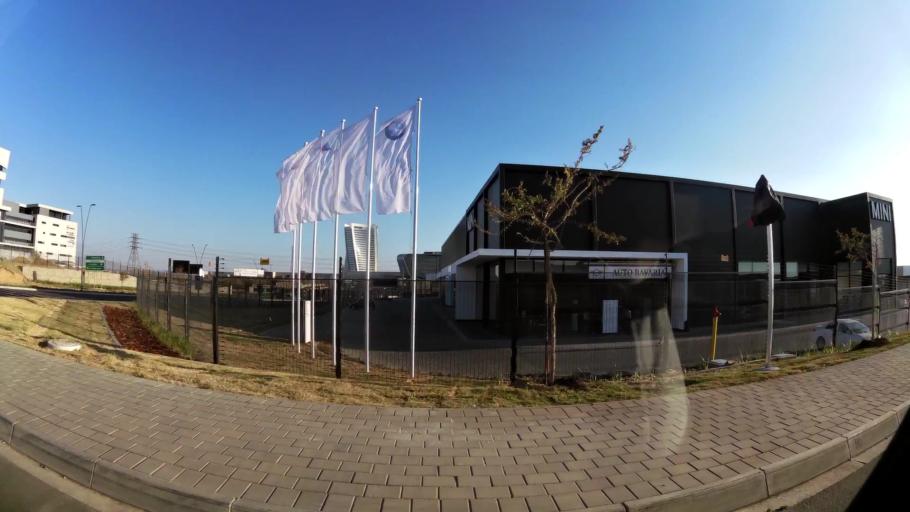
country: ZA
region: Gauteng
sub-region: City of Johannesburg Metropolitan Municipality
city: Midrand
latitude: -26.0109
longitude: 28.1097
